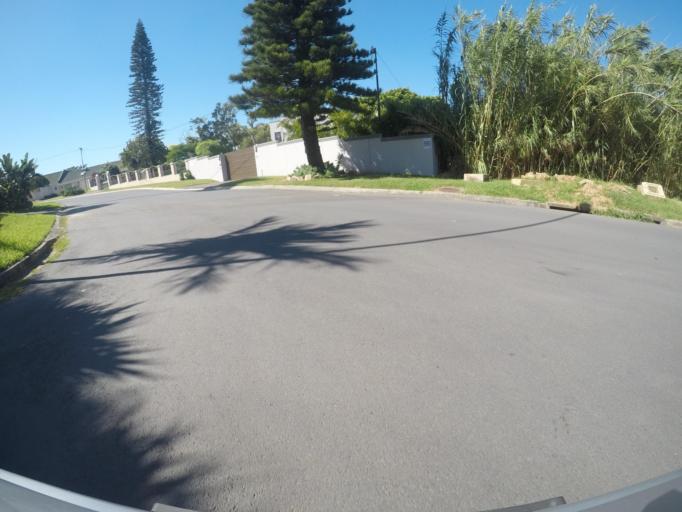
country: ZA
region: Eastern Cape
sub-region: Buffalo City Metropolitan Municipality
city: East London
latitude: -32.9557
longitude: 27.9102
